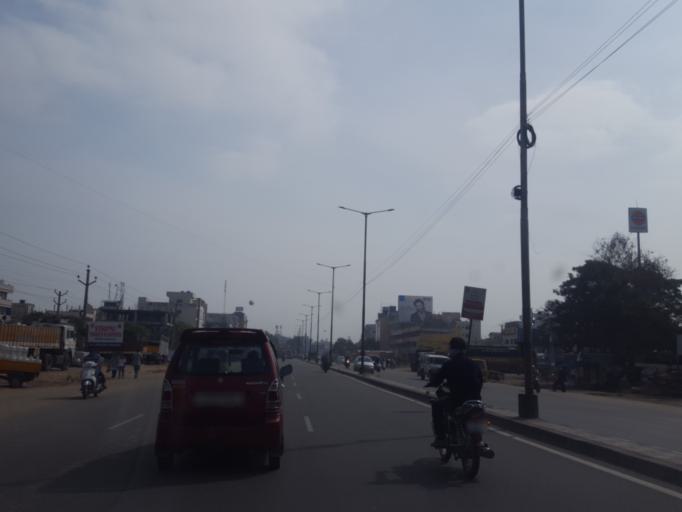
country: IN
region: Telangana
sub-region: Medak
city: Serilingampalle
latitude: 17.5108
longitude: 78.2964
